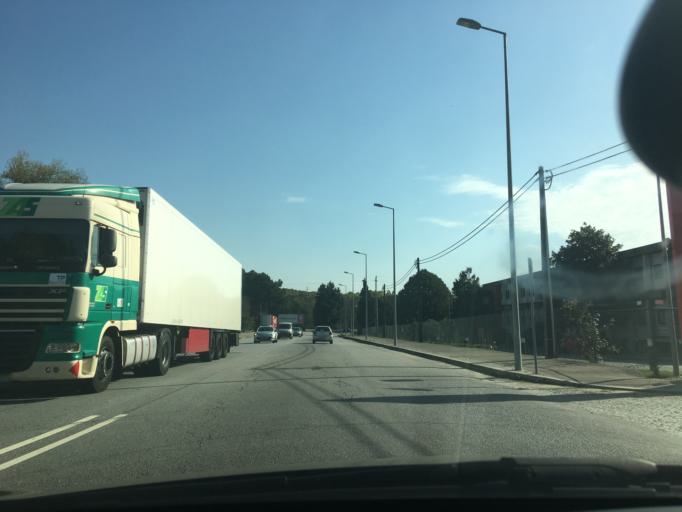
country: PT
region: Porto
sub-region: Maia
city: Maia
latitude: 41.2318
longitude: -8.6368
